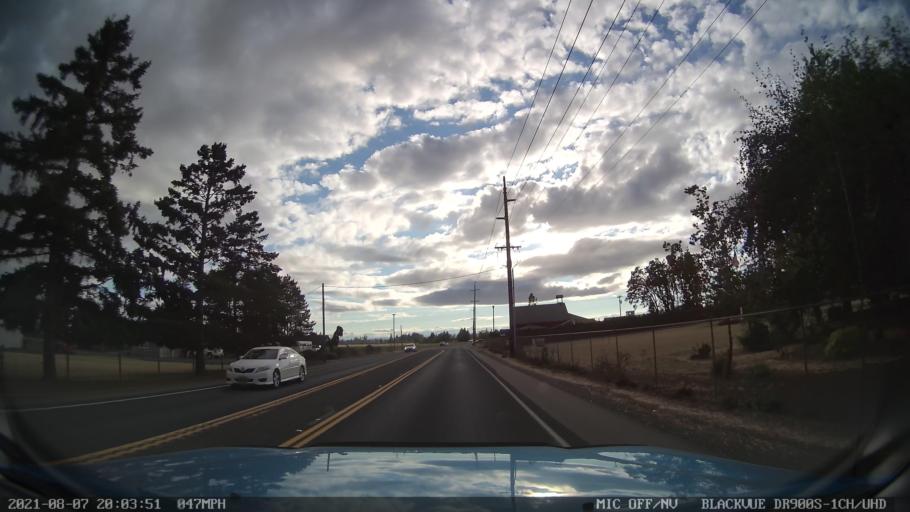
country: US
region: Oregon
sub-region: Marion County
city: Silverton
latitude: 44.9944
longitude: -122.8228
